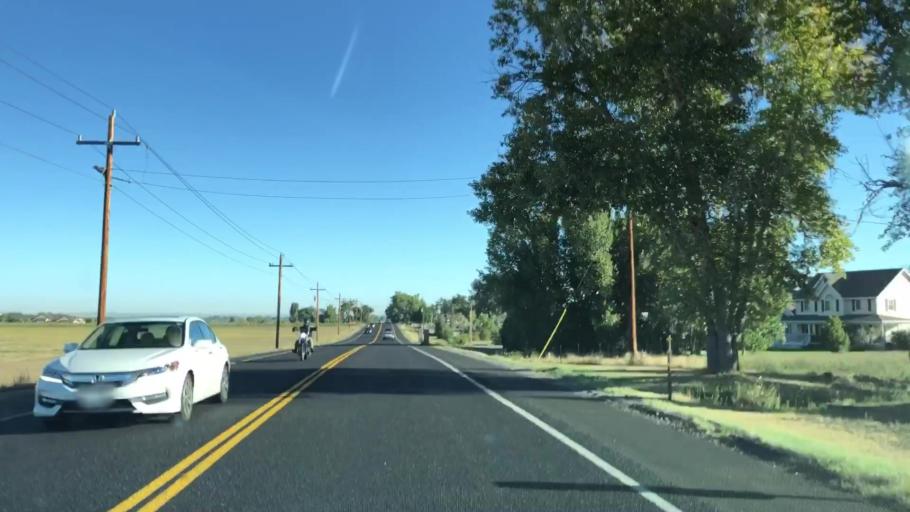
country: US
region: Colorado
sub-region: Larimer County
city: Loveland
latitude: 40.4692
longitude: -105.0395
